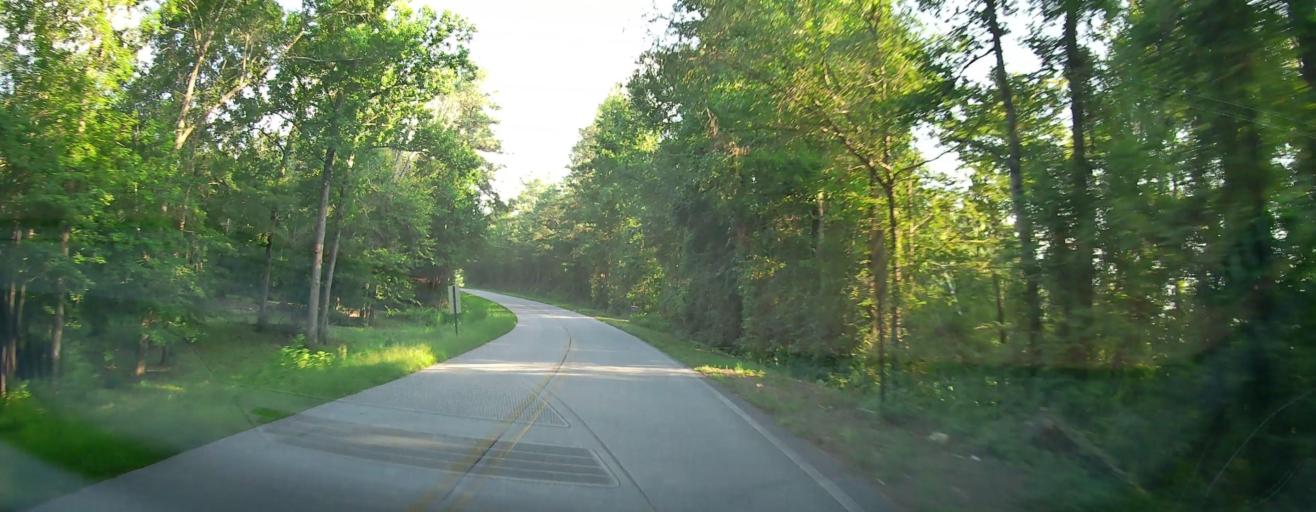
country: US
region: Georgia
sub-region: Peach County
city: Byron
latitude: 32.7149
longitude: -83.7809
